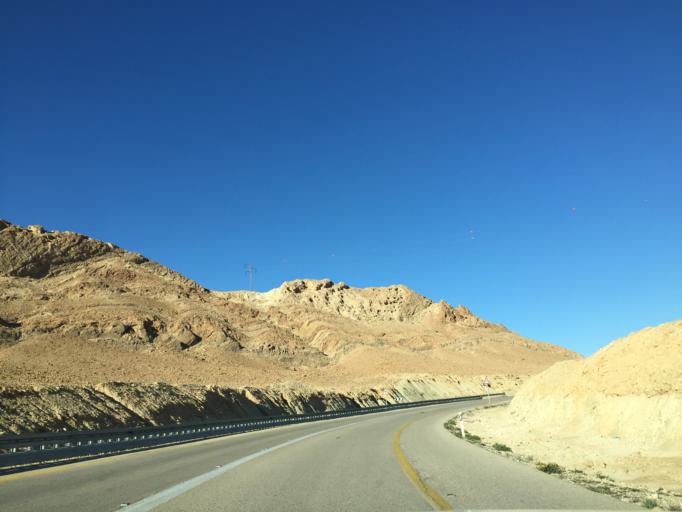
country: IL
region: Southern District
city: Mitzpe Ramon
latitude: 30.5783
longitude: 34.8834
